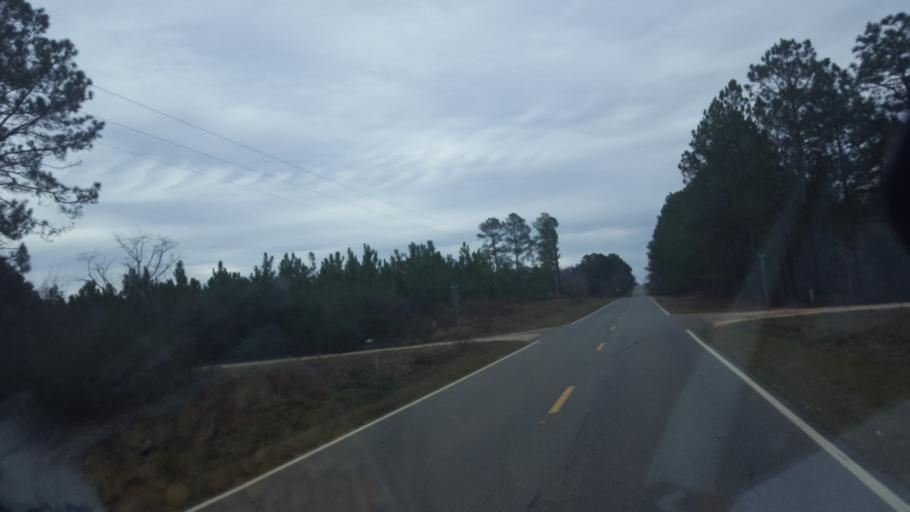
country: US
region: Georgia
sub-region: Ben Hill County
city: Fitzgerald
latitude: 31.7830
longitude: -83.4074
